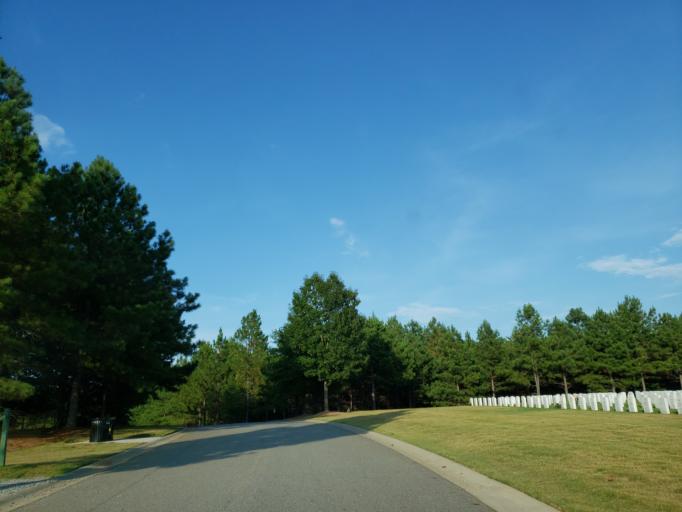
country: US
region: Georgia
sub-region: Cherokee County
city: Canton
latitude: 34.2345
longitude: -84.5833
